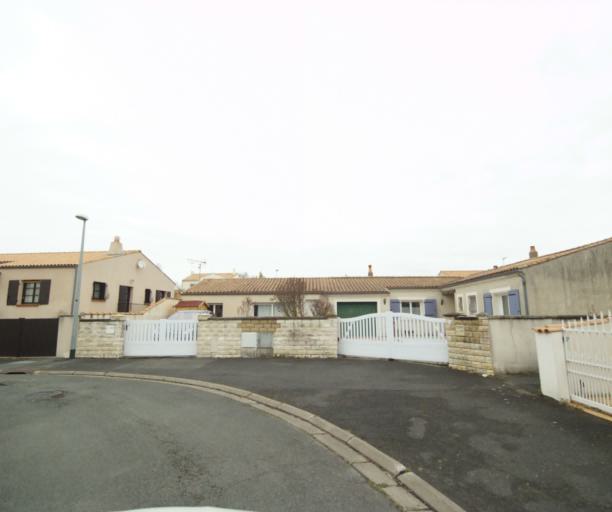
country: FR
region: Poitou-Charentes
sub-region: Departement de la Charente-Maritime
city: Lagord
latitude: 46.1926
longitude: -1.1549
